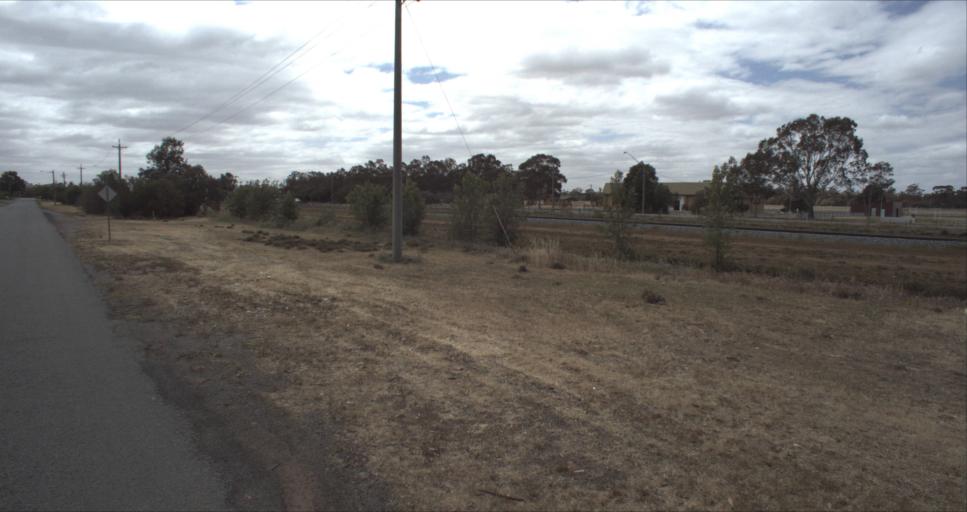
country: AU
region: New South Wales
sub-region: Leeton
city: Leeton
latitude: -34.5641
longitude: 146.3977
